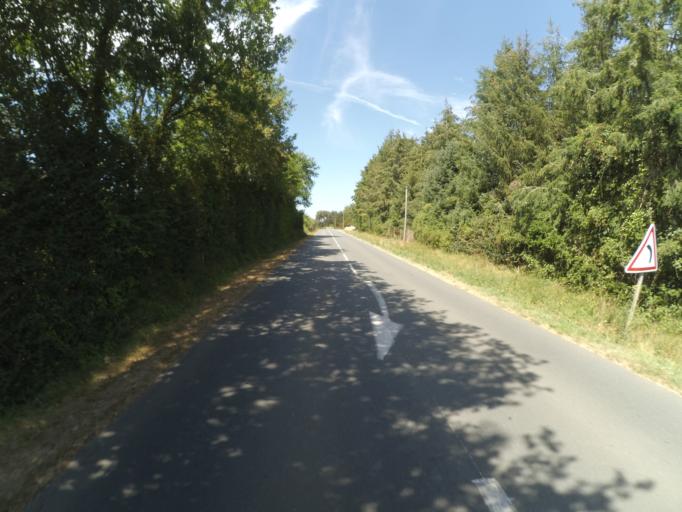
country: FR
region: Poitou-Charentes
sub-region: Departement de la Vienne
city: Saint-Maurice-la-Clouere
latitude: 46.3844
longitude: 0.4004
